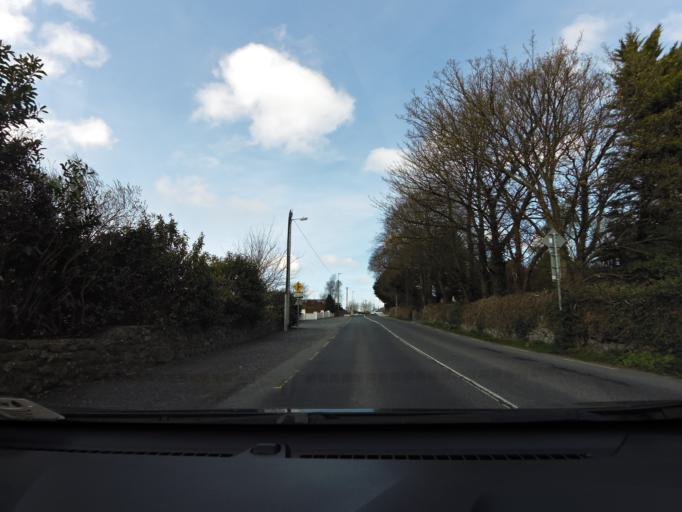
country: IE
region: Connaught
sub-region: County Galway
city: Athenry
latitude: 53.2975
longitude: -8.7566
